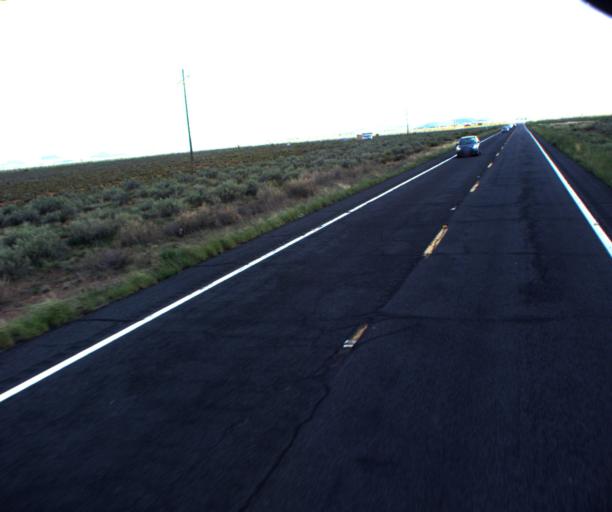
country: US
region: Arizona
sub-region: Coconino County
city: Williams
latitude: 35.6185
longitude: -112.1440
